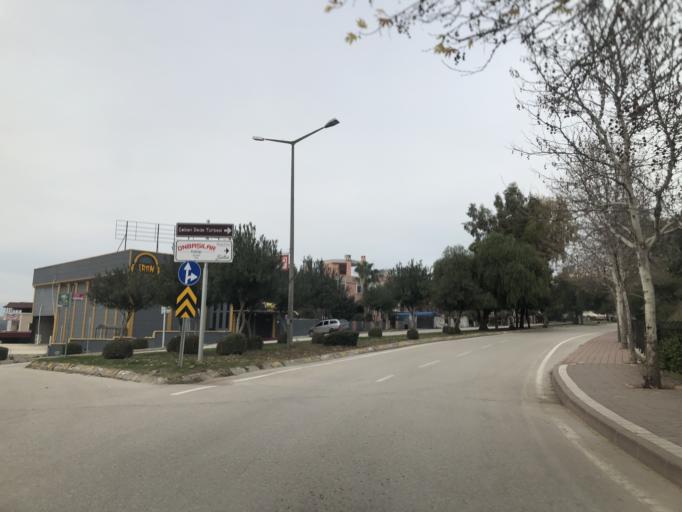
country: TR
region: Adana
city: Adana
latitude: 37.0551
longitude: 35.2962
